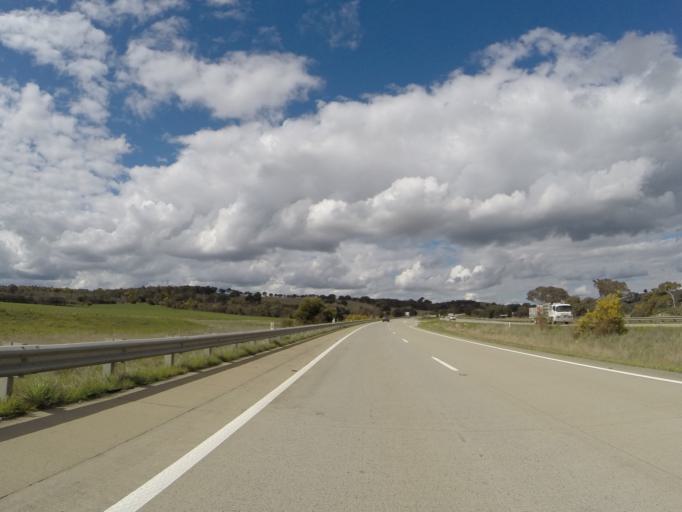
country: AU
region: New South Wales
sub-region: Yass Valley
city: Murrumbateman
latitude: -34.8009
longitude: 149.1405
